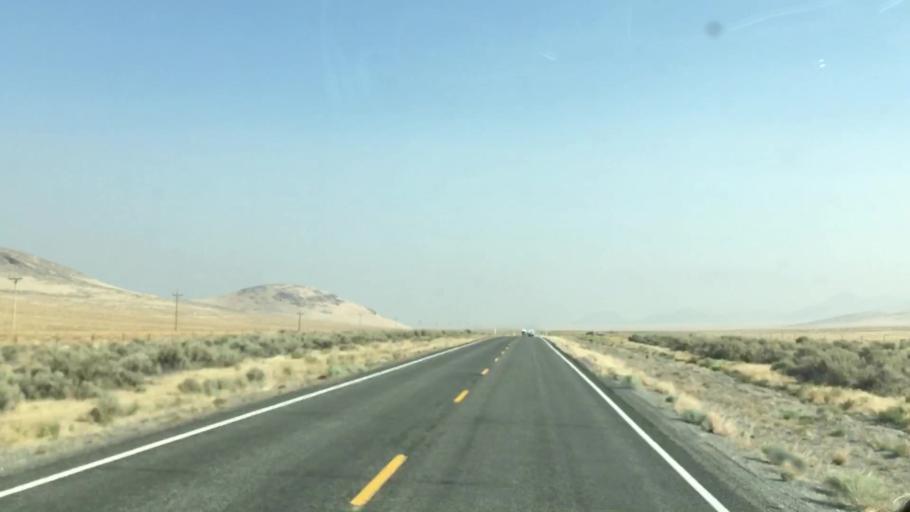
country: US
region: Nevada
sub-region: Lyon County
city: Fernley
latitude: 40.4234
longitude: -119.3339
